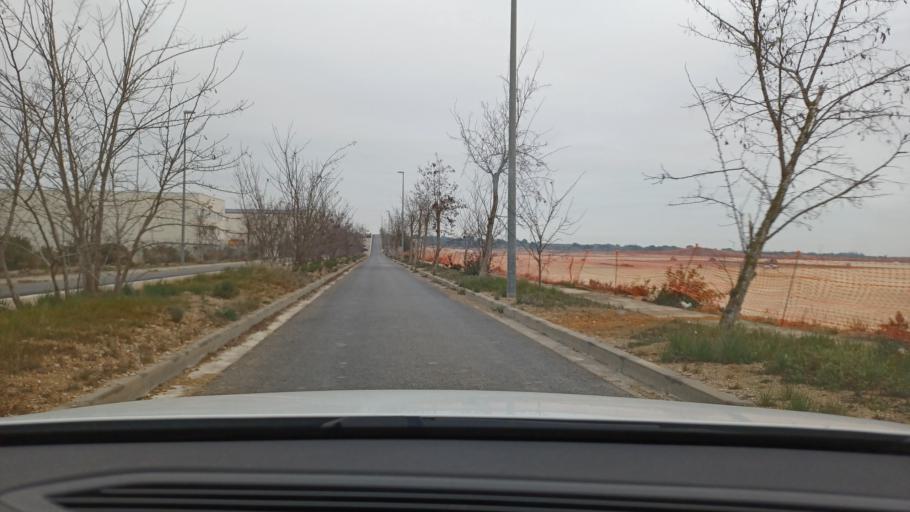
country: ES
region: Catalonia
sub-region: Provincia de Tarragona
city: Amposta
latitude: 40.7635
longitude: 0.5902
